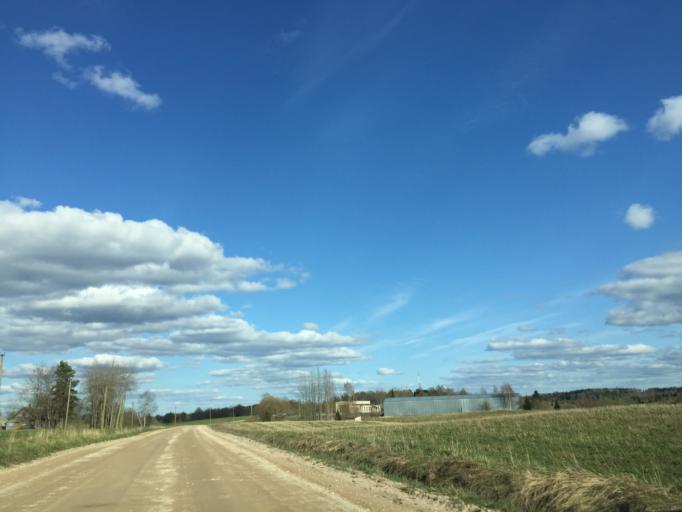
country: LV
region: Rezekne
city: Rezekne
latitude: 56.6487
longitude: 27.3582
